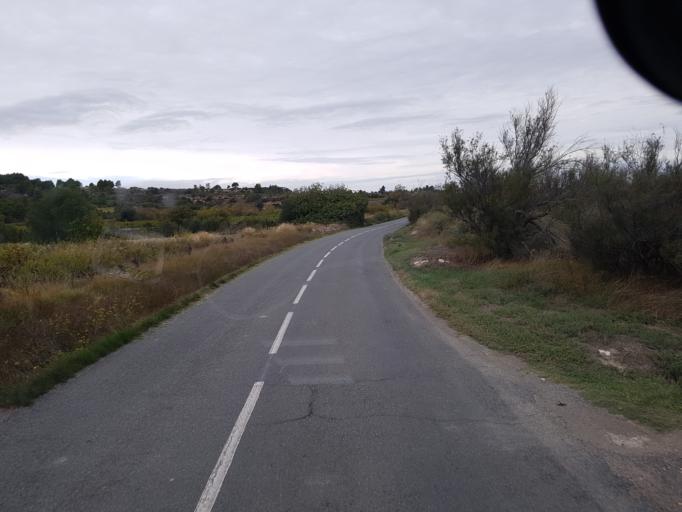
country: FR
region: Languedoc-Roussillon
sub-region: Departement de l'Aude
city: Peyriac-de-Mer
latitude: 43.1249
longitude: 2.9873
